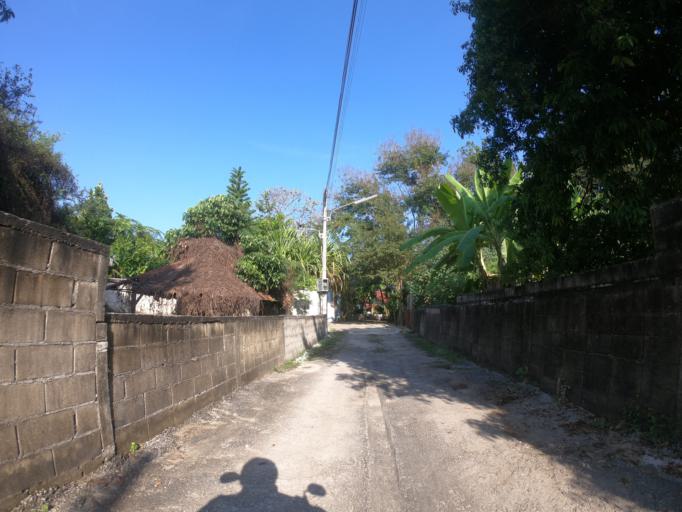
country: TH
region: Chiang Mai
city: Chiang Mai
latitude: 18.7557
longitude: 98.9929
